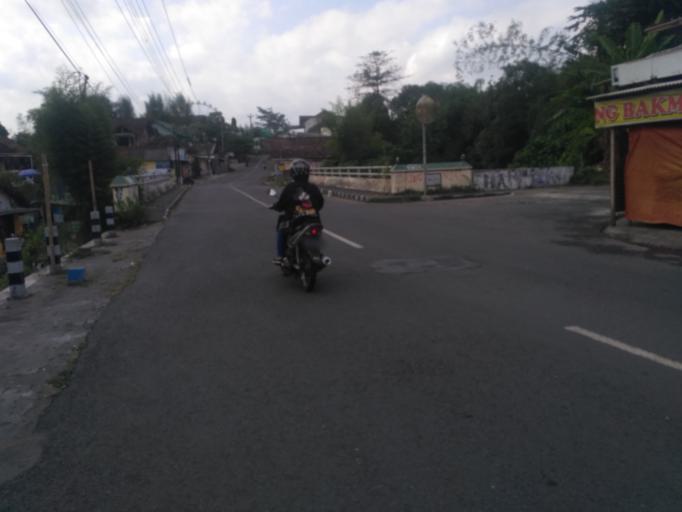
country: ID
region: Daerah Istimewa Yogyakarta
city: Yogyakarta
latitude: -7.7663
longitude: 110.3517
